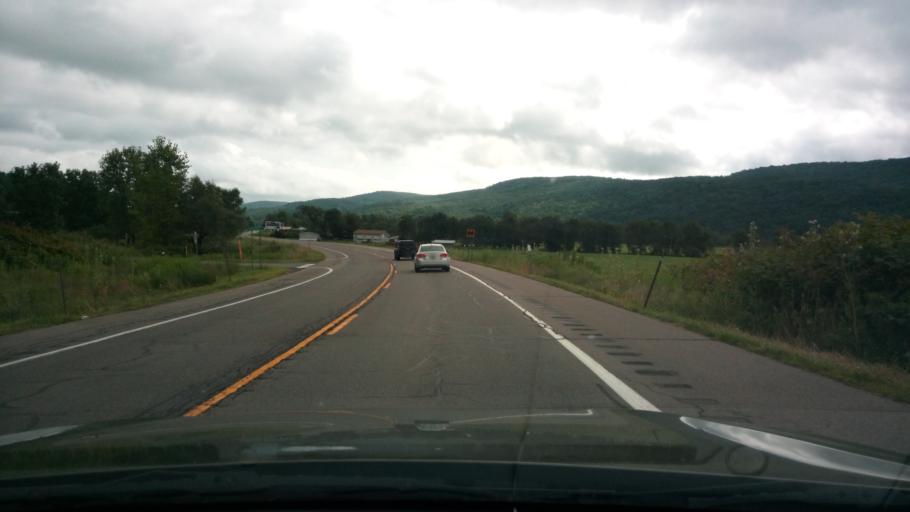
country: US
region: New York
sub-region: Chemung County
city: Horseheads North
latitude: 42.2915
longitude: -76.7000
